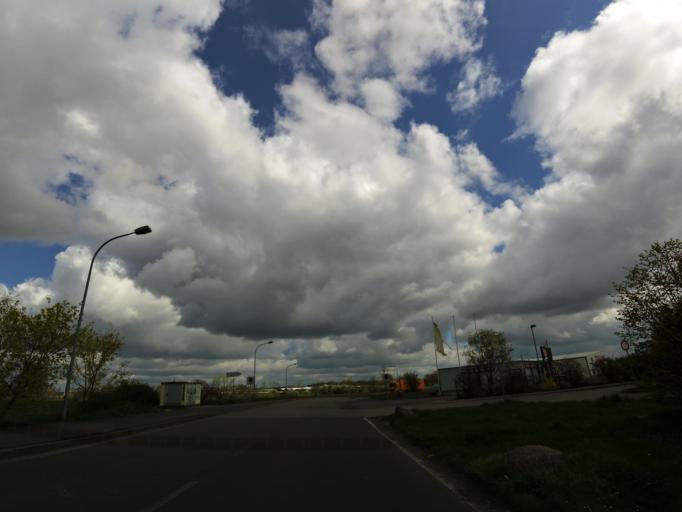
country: DE
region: Saxony-Anhalt
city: Loburg
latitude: 52.2370
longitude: 12.0589
